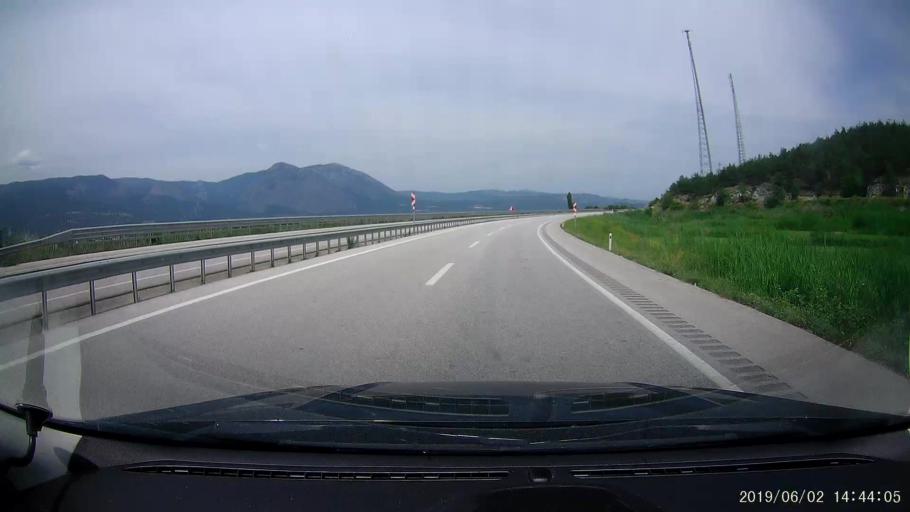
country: TR
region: Corum
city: Hacihamza
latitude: 41.1012
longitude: 34.4050
